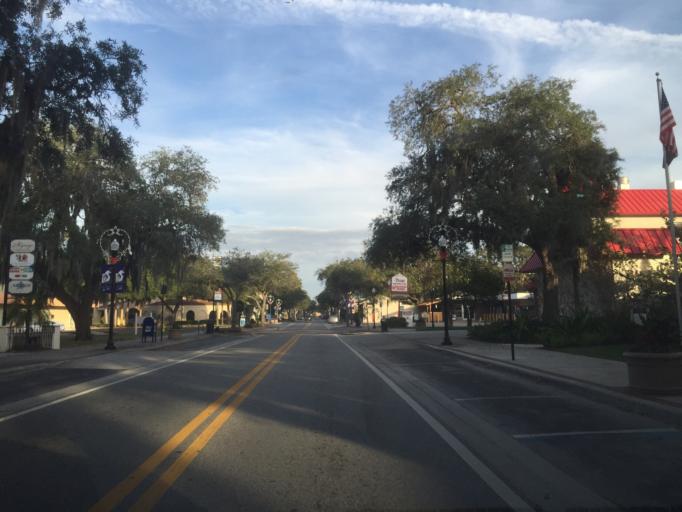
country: US
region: Florida
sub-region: Pinellas County
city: Safety Harbor
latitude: 27.9908
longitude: -82.6949
